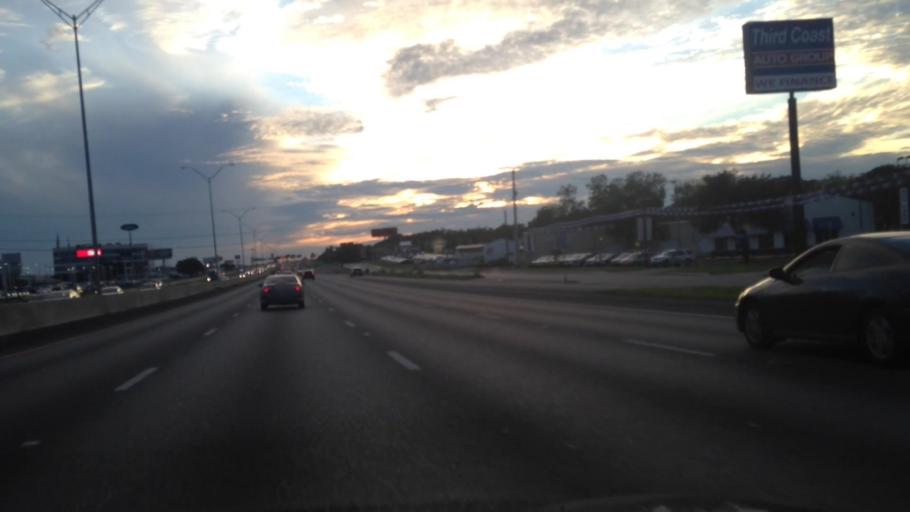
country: US
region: Texas
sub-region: Comal County
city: New Braunfels
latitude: 29.6890
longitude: -98.1122
